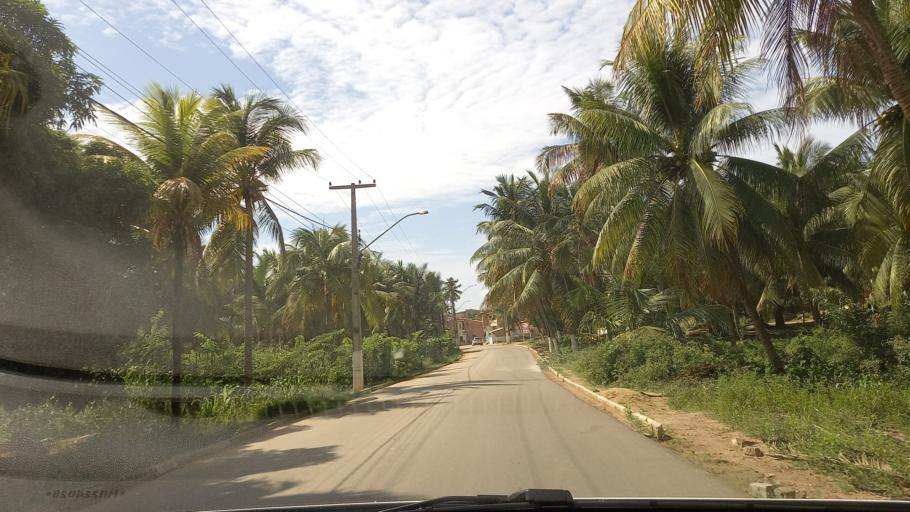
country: BR
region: Alagoas
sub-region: Maragogi
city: Maragogi
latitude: -9.0039
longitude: -35.2201
